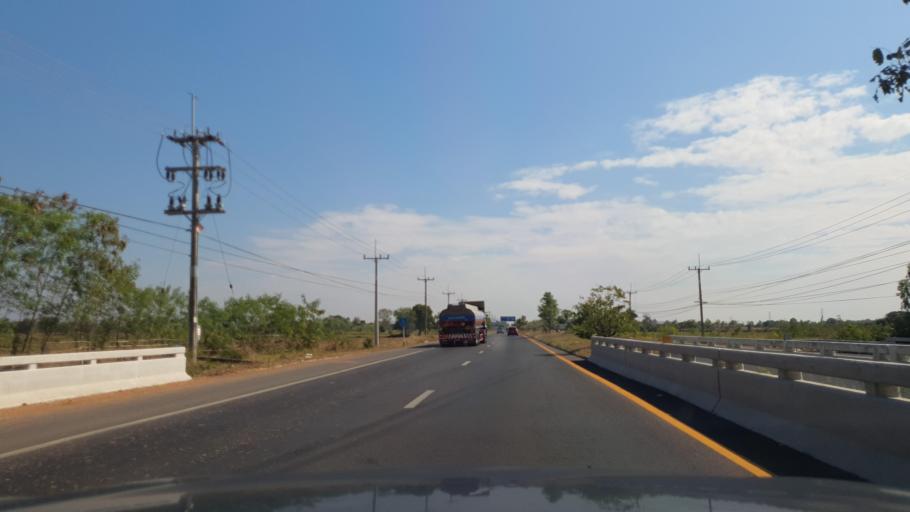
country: TH
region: Maha Sarakham
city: Chiang Yuen
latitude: 16.3759
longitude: 103.1677
